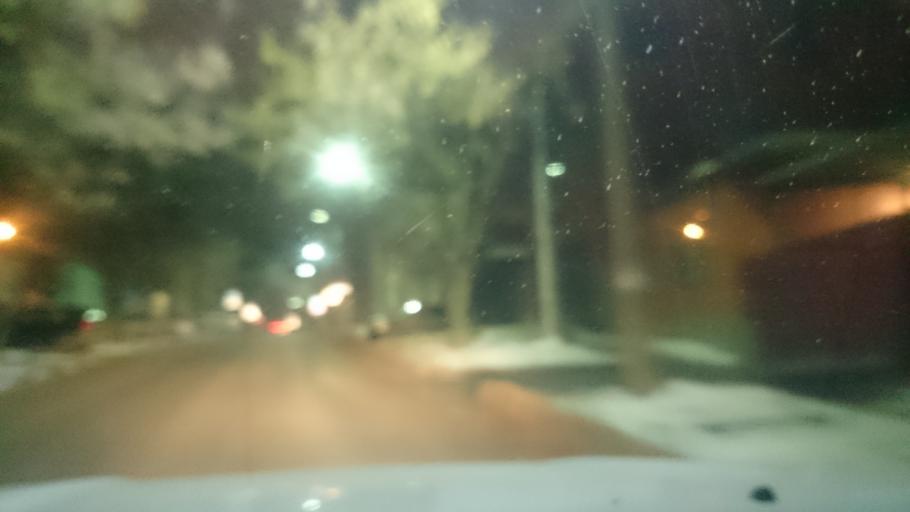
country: RU
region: Tula
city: Tula
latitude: 54.1842
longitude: 37.6156
